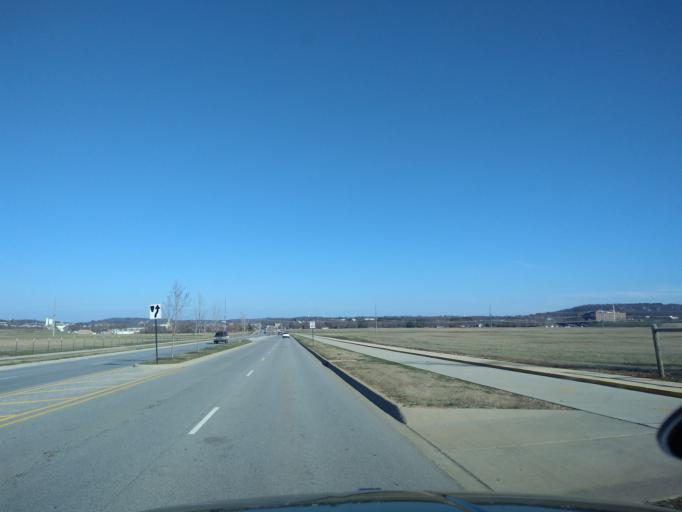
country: US
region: Arkansas
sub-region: Washington County
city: Johnson
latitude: 36.1172
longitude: -94.1740
